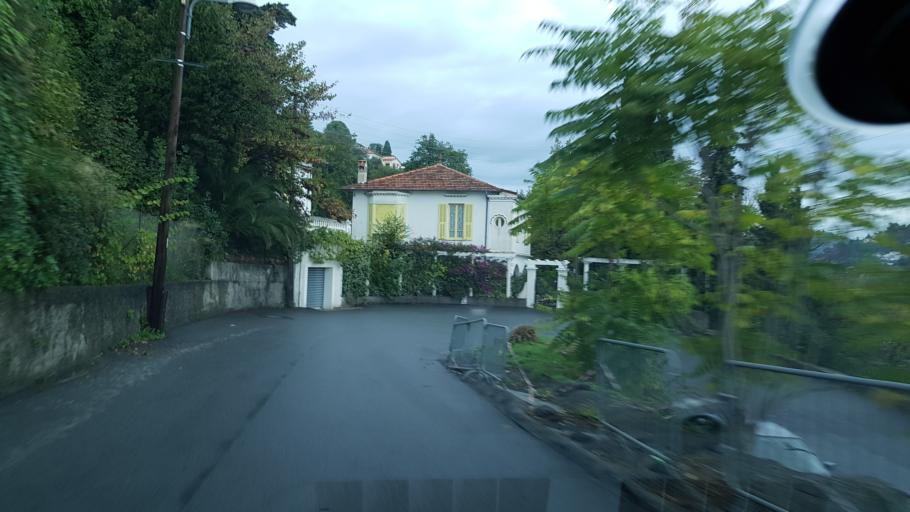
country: FR
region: Provence-Alpes-Cote d'Azur
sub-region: Departement des Alpes-Maritimes
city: Nice
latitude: 43.6987
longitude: 7.2364
